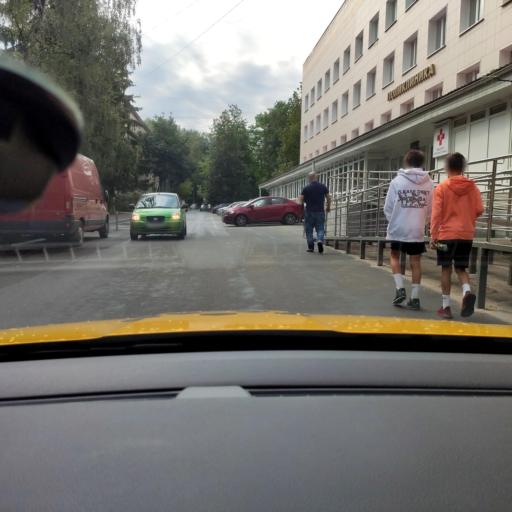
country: RU
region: Moskovskaya
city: Troitsk
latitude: 55.4728
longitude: 37.3006
